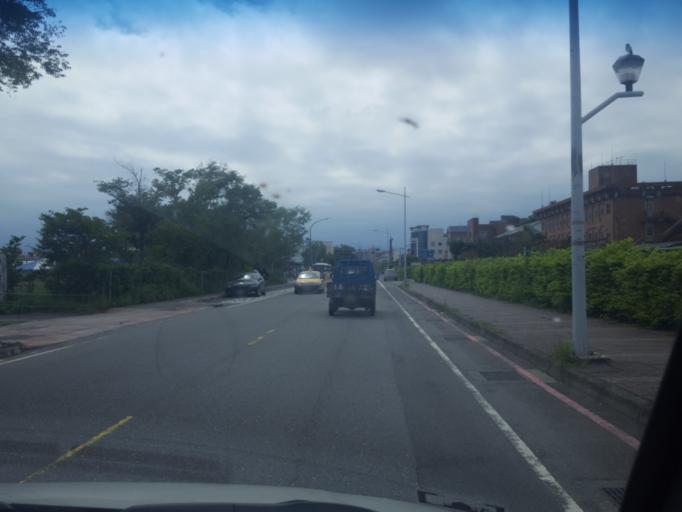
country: TW
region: Taiwan
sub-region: Yilan
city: Yilan
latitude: 24.7535
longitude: 121.7591
